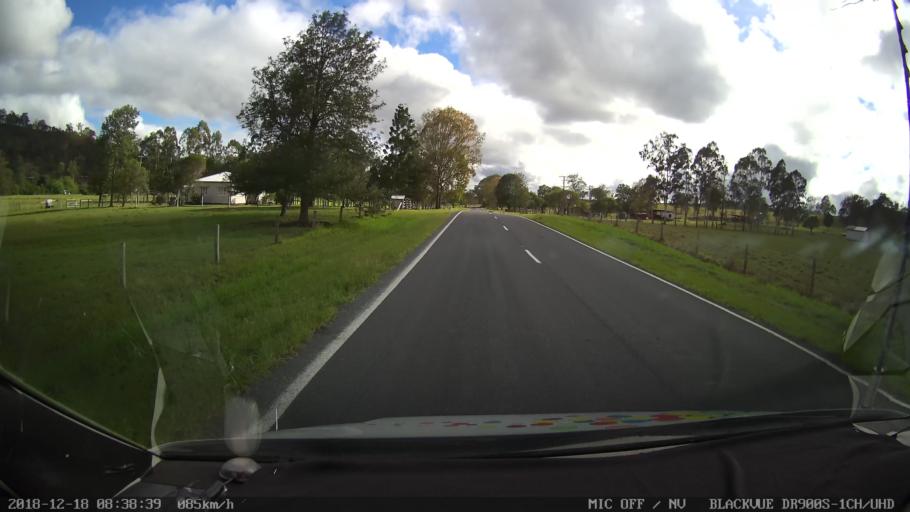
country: AU
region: New South Wales
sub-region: Kyogle
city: Kyogle
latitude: -28.2544
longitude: 152.8300
